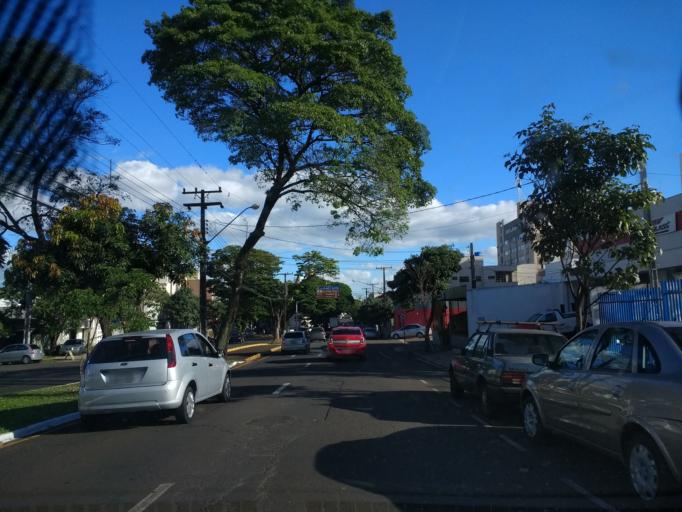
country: BR
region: Parana
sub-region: Londrina
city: Londrina
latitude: -23.3247
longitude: -51.1551
